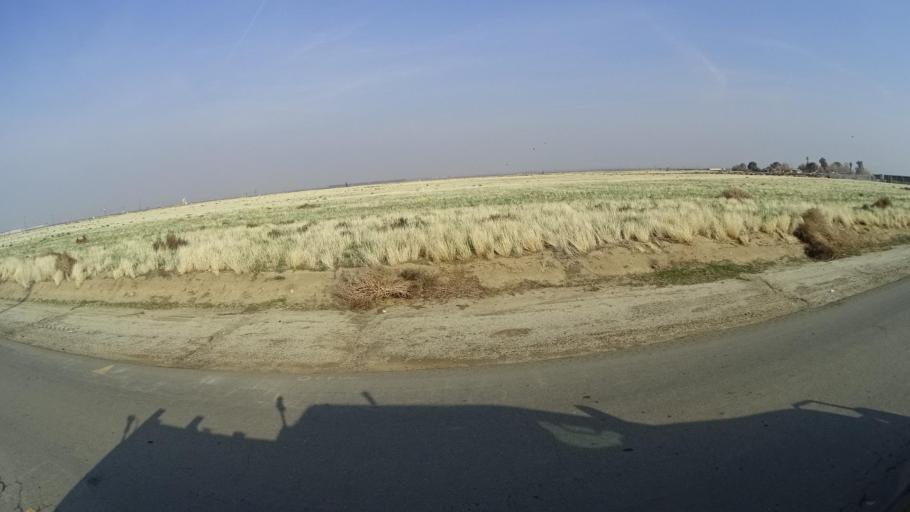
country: US
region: California
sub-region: Kern County
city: Lebec
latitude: 34.9839
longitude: -118.9155
